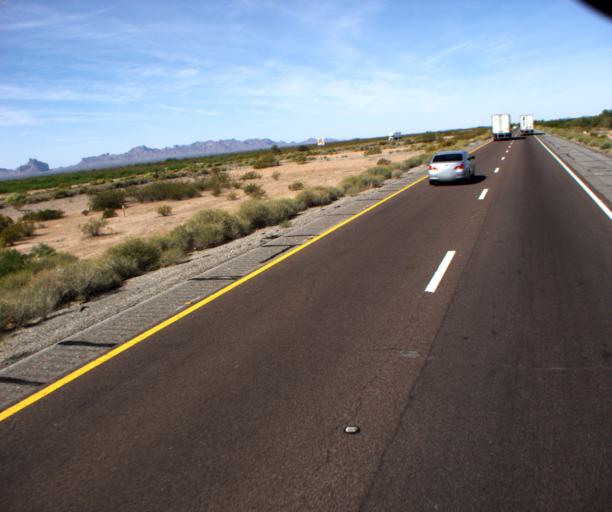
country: US
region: Arizona
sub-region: La Paz County
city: Salome
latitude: 33.5478
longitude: -113.2118
